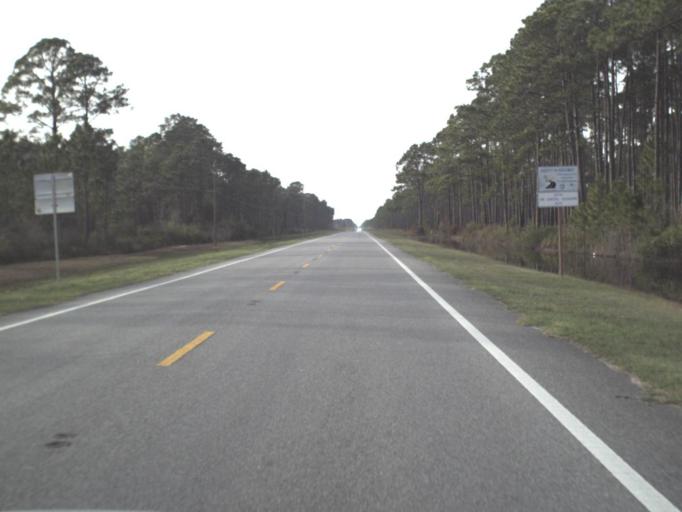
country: US
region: Florida
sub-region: Bay County
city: Mexico Beach
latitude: 30.0115
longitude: -85.5143
